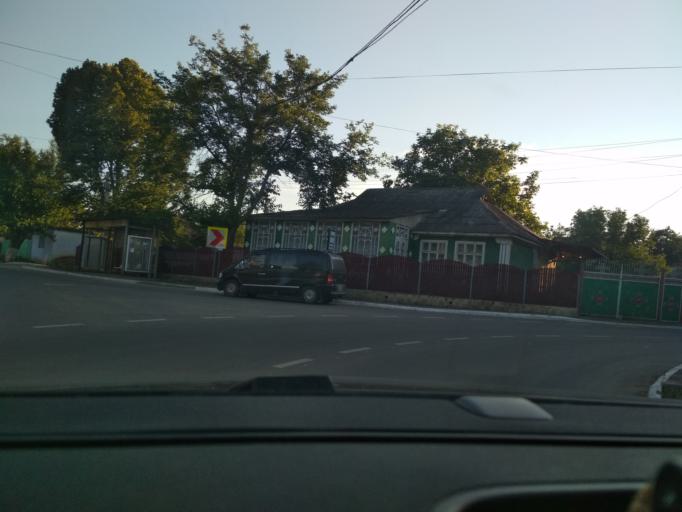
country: RO
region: Iasi
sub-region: Comuna Grozesti
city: Grozesti
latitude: 46.9683
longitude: 28.1060
